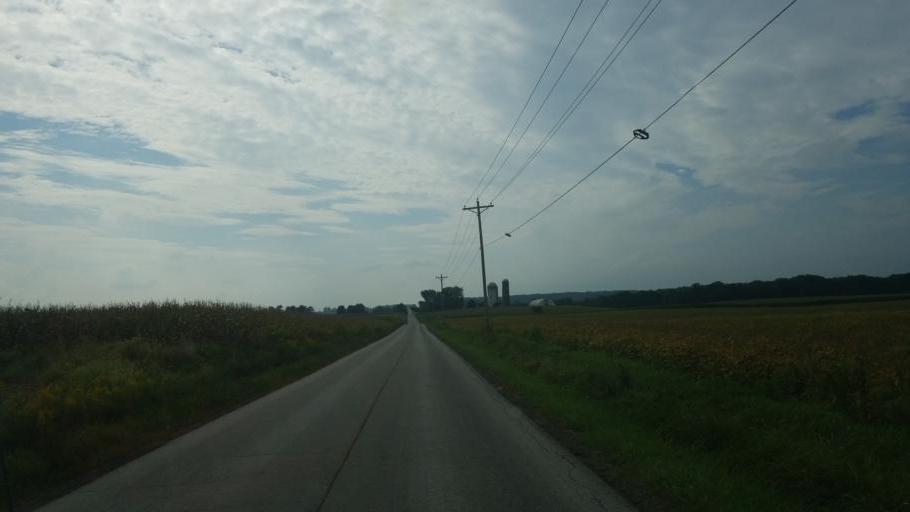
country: US
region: Ohio
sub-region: Wayne County
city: West Salem
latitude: 40.9158
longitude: -82.0294
